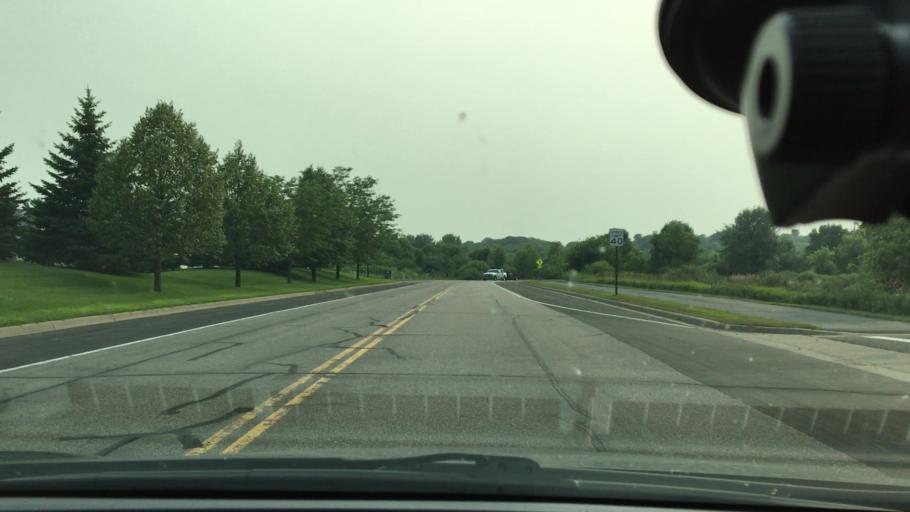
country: US
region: Minnesota
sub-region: Wright County
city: Otsego
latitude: 45.2623
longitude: -93.5764
